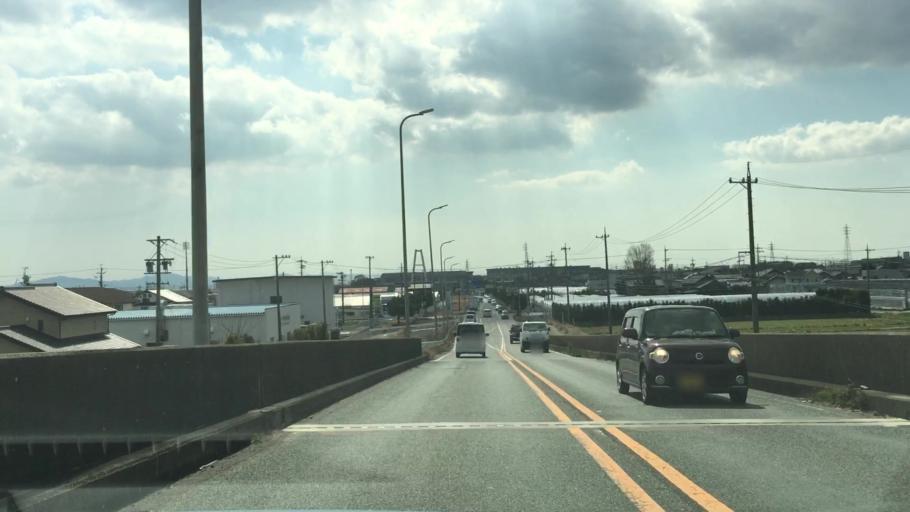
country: JP
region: Aichi
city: Kozakai-cho
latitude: 34.8130
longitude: 137.3123
